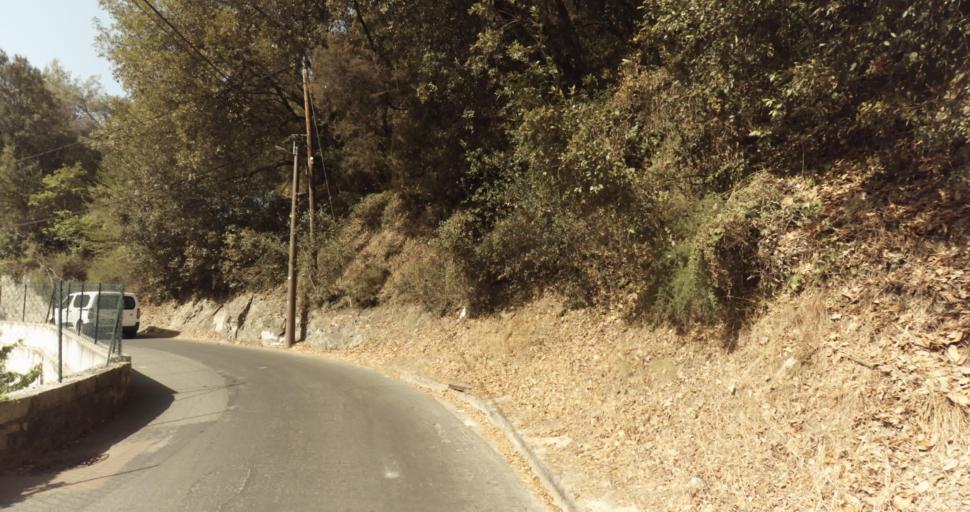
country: FR
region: Provence-Alpes-Cote d'Azur
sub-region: Departement des Alpes-Maritimes
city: Sainte-Agnes
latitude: 43.7914
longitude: 7.4808
